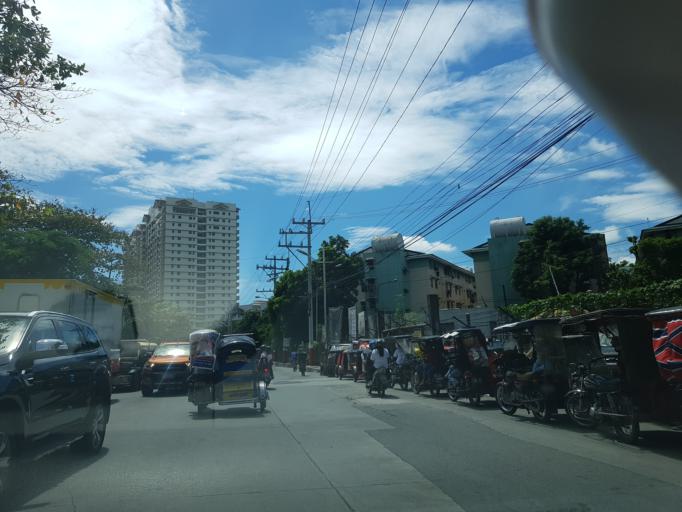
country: PH
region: Calabarzon
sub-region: Province of Rizal
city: Pateros
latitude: 14.5296
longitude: 121.0609
